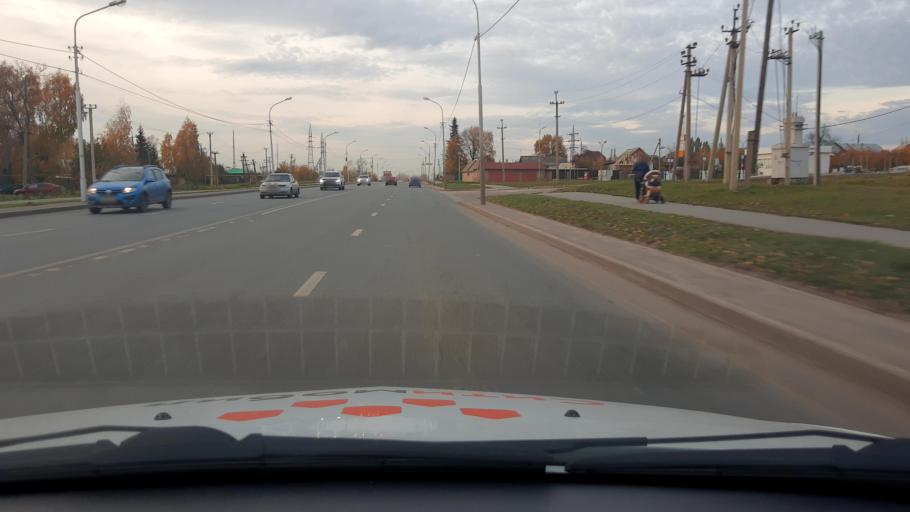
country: RU
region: Bashkortostan
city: Iglino
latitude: 54.7786
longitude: 56.2291
